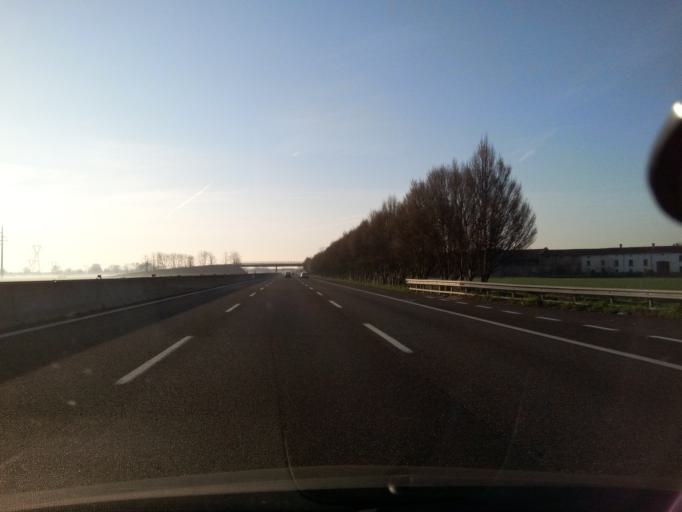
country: IT
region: Lombardy
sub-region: Provincia di Lodi
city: Fombio
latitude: 45.1231
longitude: 9.6689
